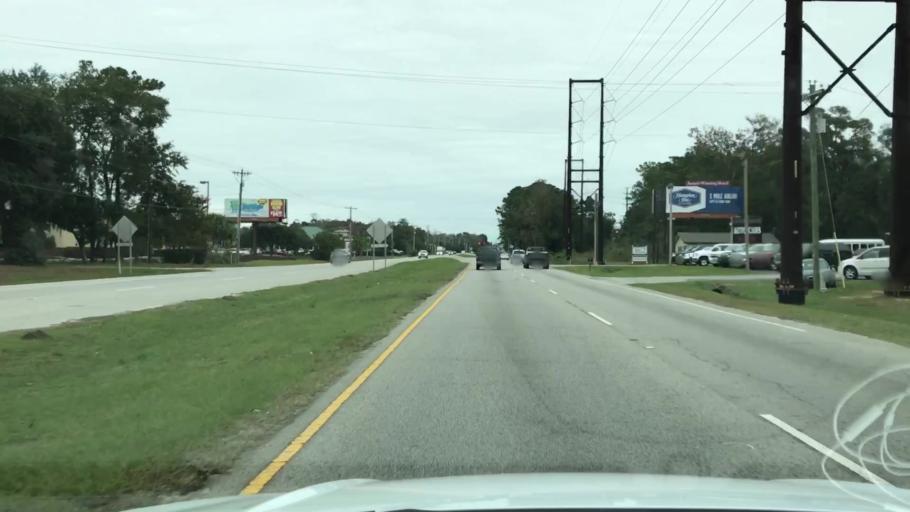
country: US
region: South Carolina
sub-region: Georgetown County
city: Murrells Inlet
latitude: 33.5519
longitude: -79.0468
